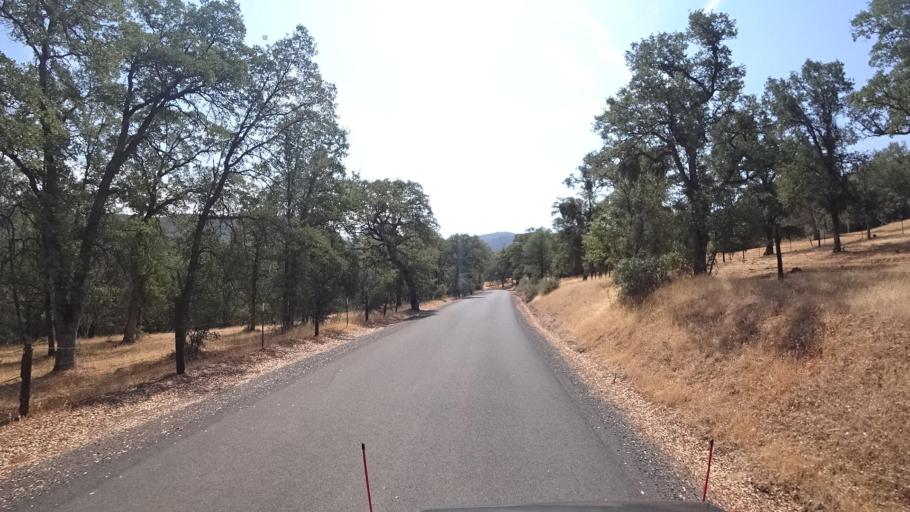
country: US
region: California
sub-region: Tuolumne County
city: Tuolumne City
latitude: 37.7119
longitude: -120.1794
